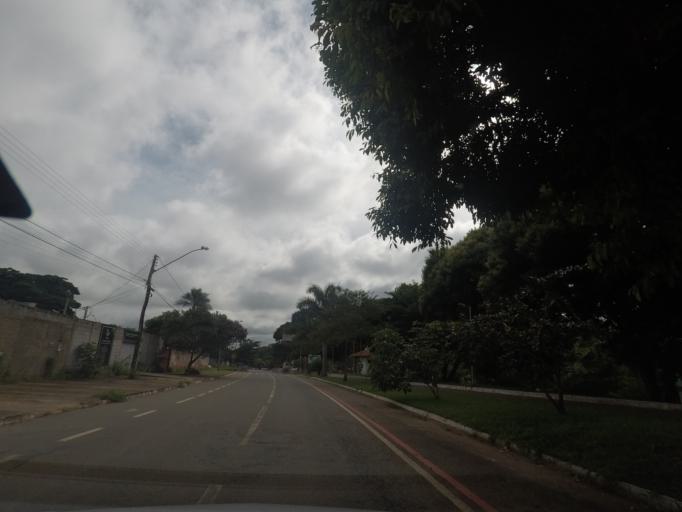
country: BR
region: Goias
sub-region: Goiania
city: Goiania
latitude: -16.7240
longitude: -49.2534
